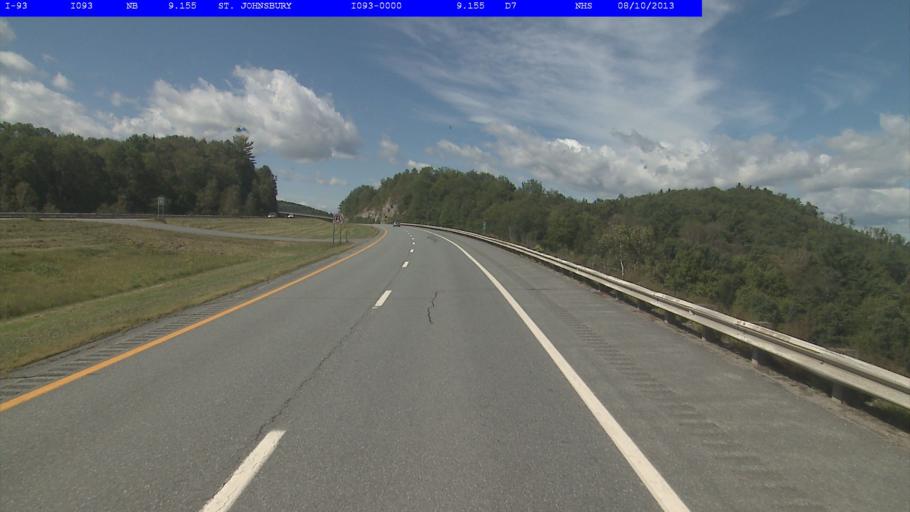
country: US
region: Vermont
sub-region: Caledonia County
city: Saint Johnsbury
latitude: 44.4151
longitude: -71.9841
